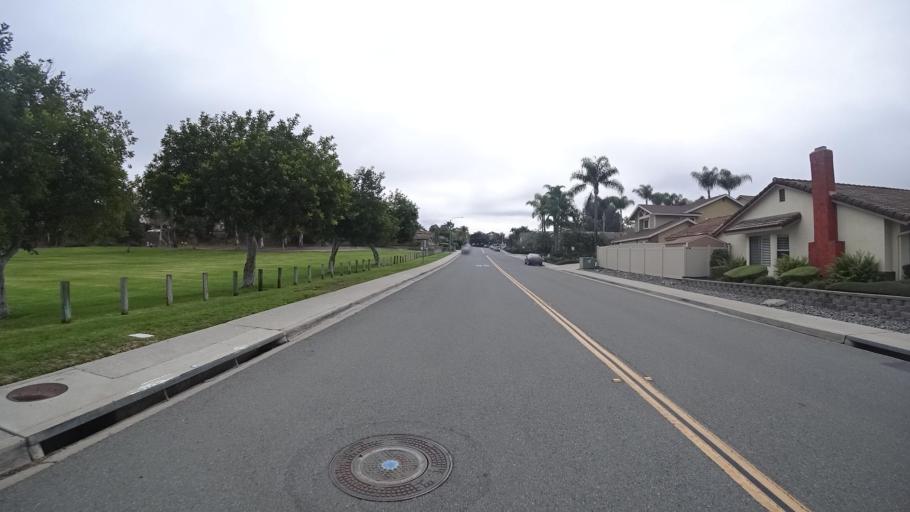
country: US
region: California
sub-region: San Diego County
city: Rancho San Diego
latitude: 32.7512
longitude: -116.9163
